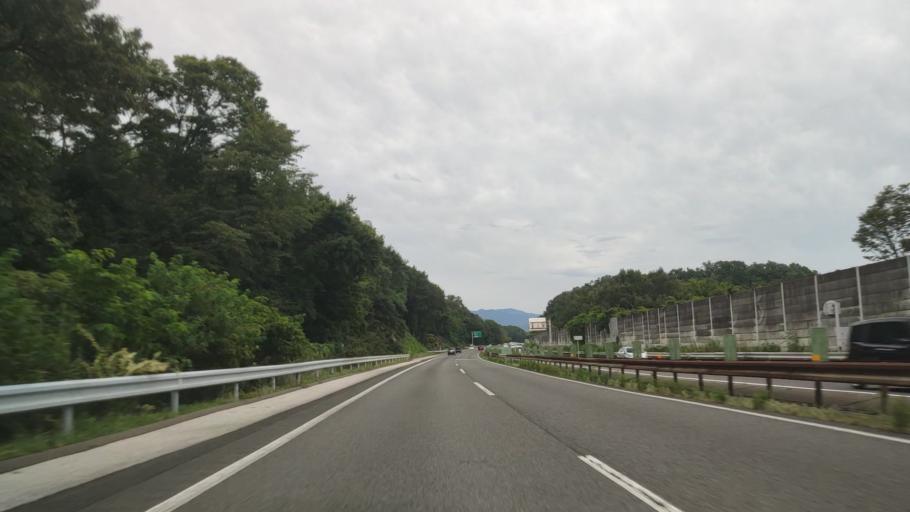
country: JP
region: Shiga Prefecture
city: Hikone
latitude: 35.2530
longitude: 136.2805
